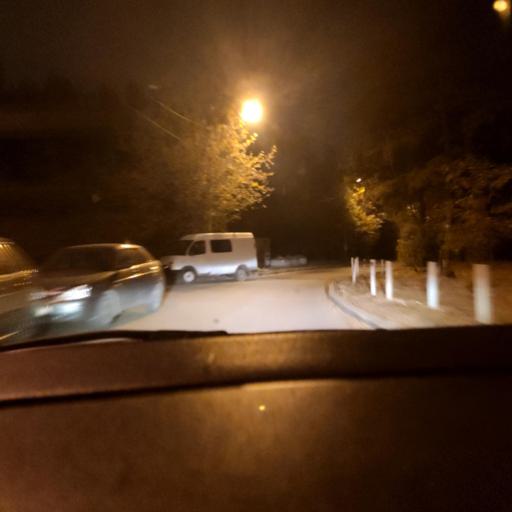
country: RU
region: Voronezj
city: Podgornoye
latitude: 51.6844
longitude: 39.1317
